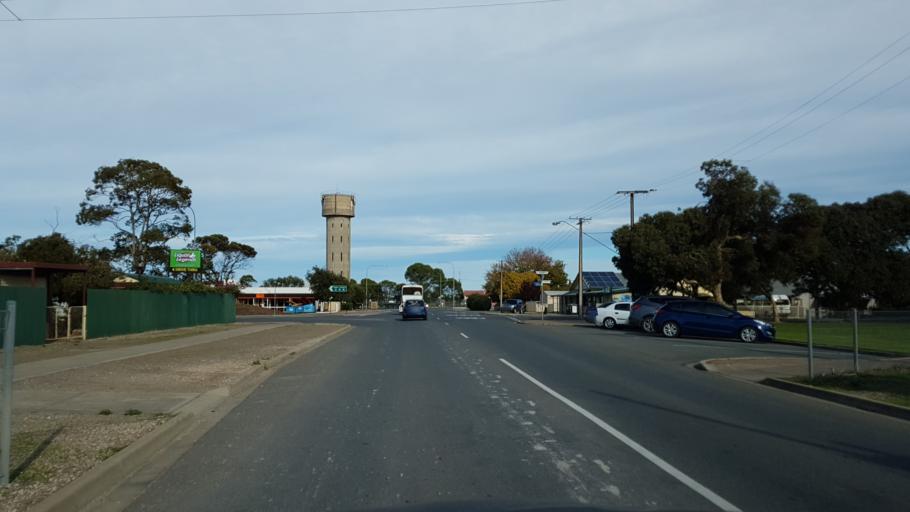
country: AU
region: South Australia
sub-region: Murray Bridge
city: Tailem Bend
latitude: -35.2526
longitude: 139.4540
